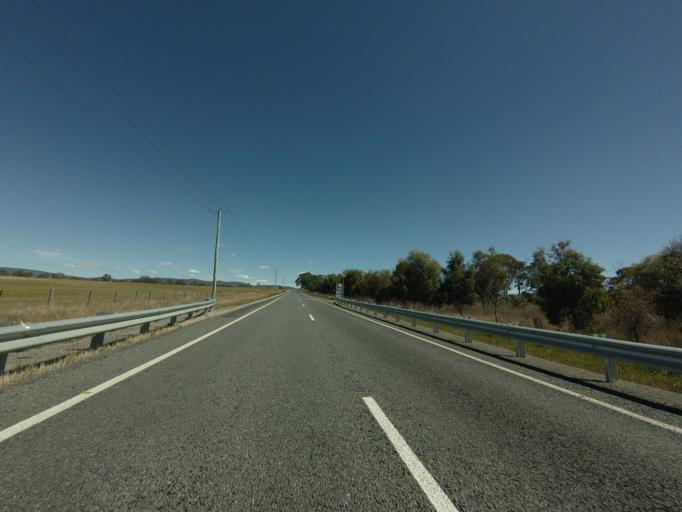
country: AU
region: Tasmania
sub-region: Northern Midlands
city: Evandale
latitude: -41.7697
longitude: 147.7398
